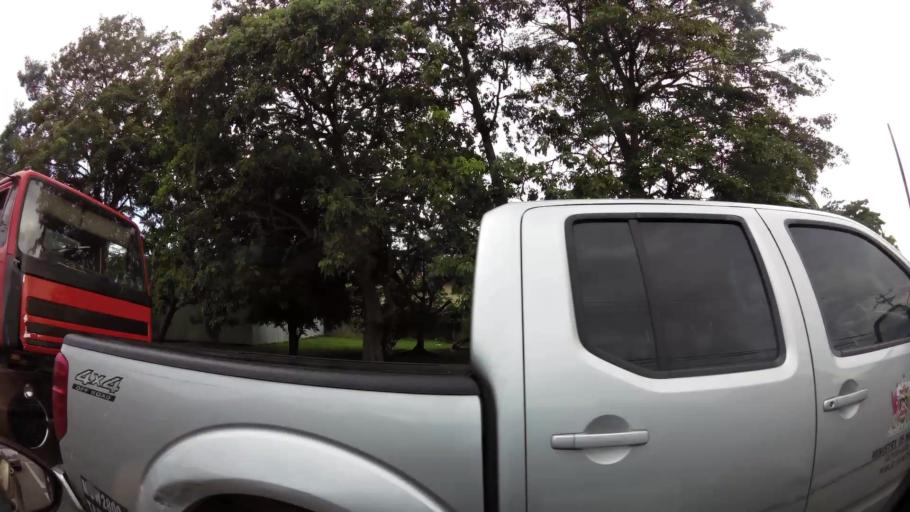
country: TT
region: Tunapuna/Piarco
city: Tunapuna
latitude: 10.6506
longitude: -61.4371
